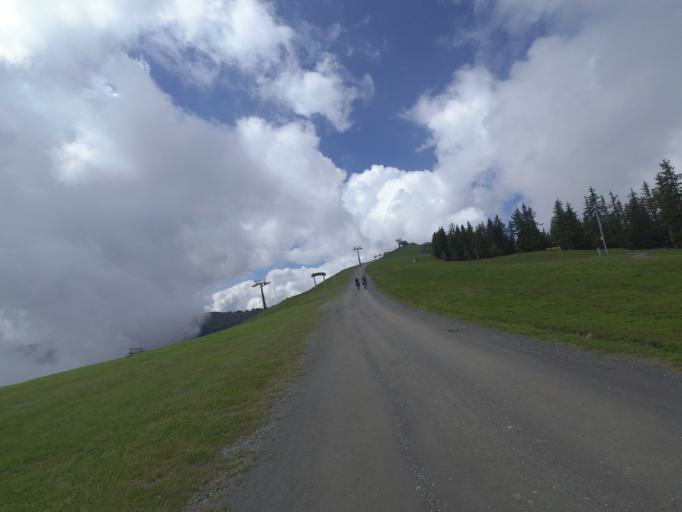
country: AT
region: Salzburg
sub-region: Politischer Bezirk Zell am See
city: Viehhofen
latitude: 47.4089
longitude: 12.7112
